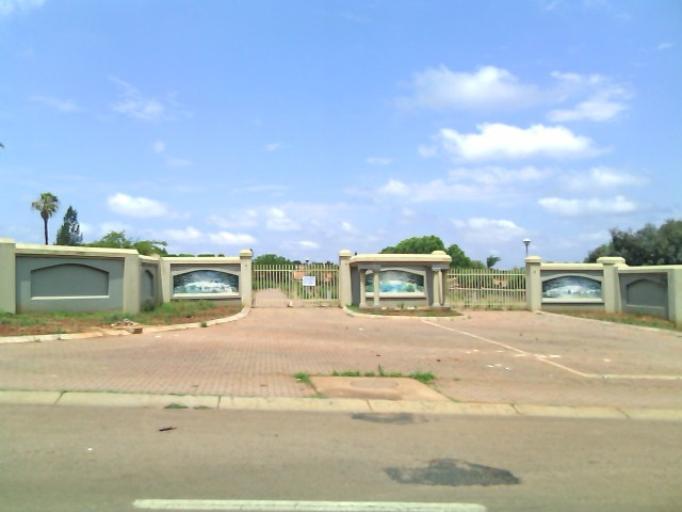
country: ZA
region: Gauteng
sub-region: City of Tshwane Metropolitan Municipality
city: Centurion
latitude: -25.8408
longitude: 28.1974
